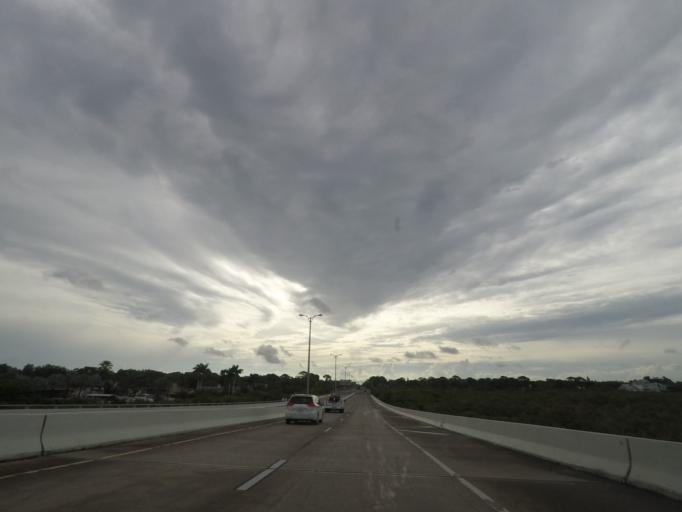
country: US
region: Florida
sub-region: Pinellas County
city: Redington Shores
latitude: 27.8439
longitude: -82.8371
